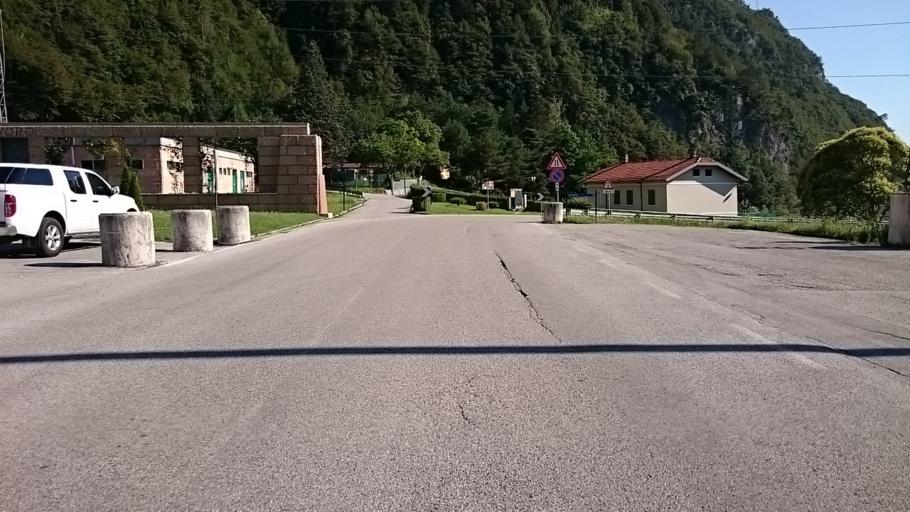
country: IT
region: Veneto
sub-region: Provincia di Belluno
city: Soverzene
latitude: 46.2010
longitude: 12.3019
